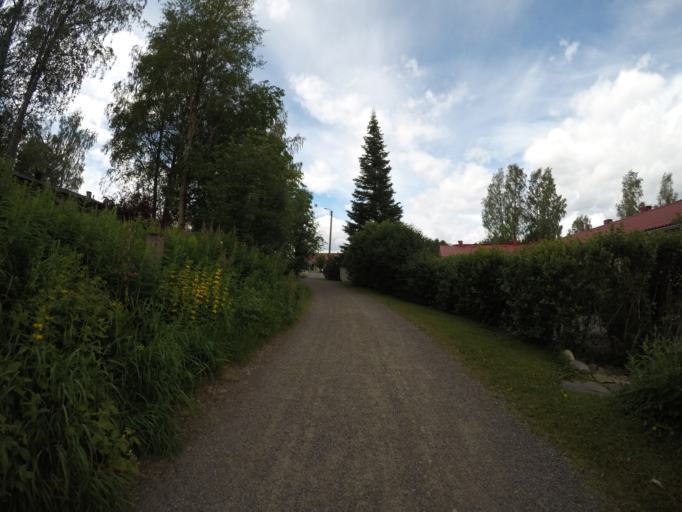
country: FI
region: Haeme
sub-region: Haemeenlinna
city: Haemeenlinna
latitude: 60.9750
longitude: 24.4339
